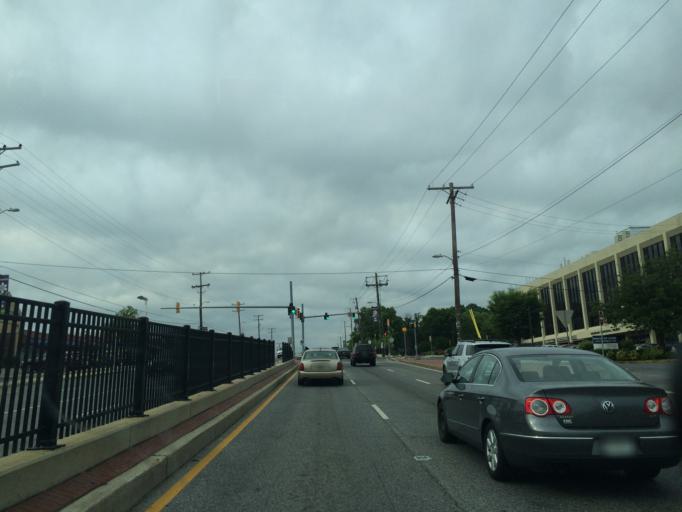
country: US
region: Maryland
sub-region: Prince George's County
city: Langley Park
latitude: 38.9884
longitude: -76.9879
